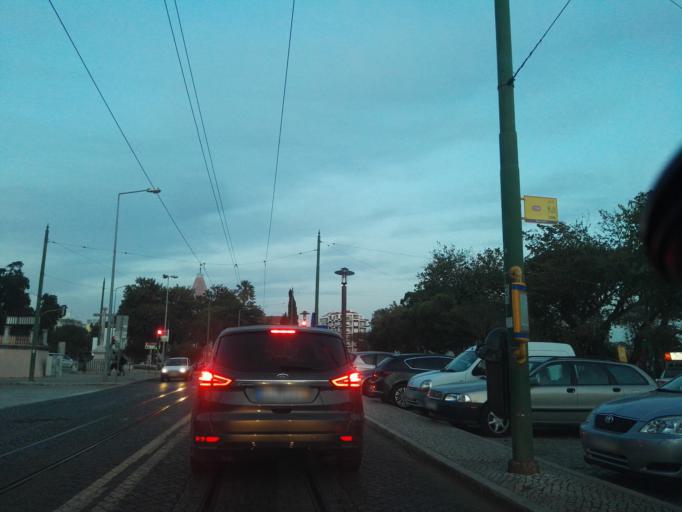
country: PT
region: Lisbon
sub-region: Oeiras
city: Alges
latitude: 38.6994
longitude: -9.2321
